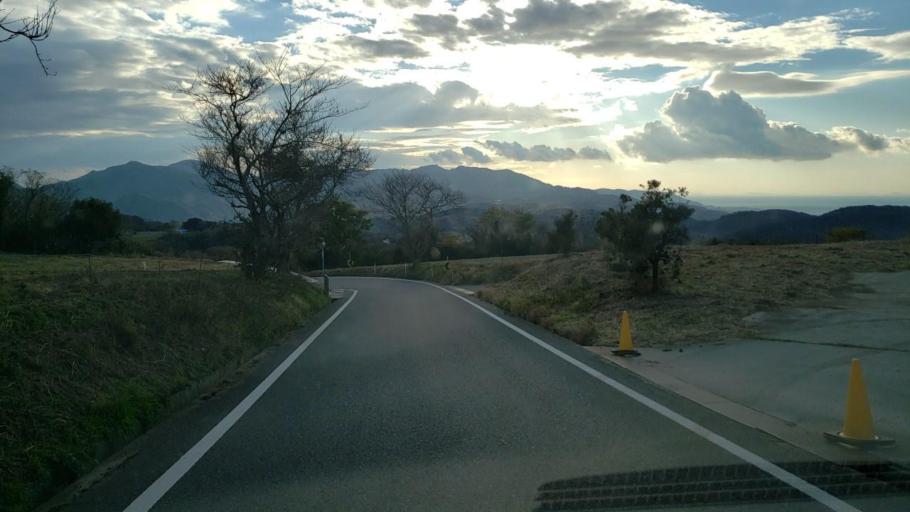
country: JP
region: Hyogo
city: Akashi
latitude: 34.5515
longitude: 134.9761
